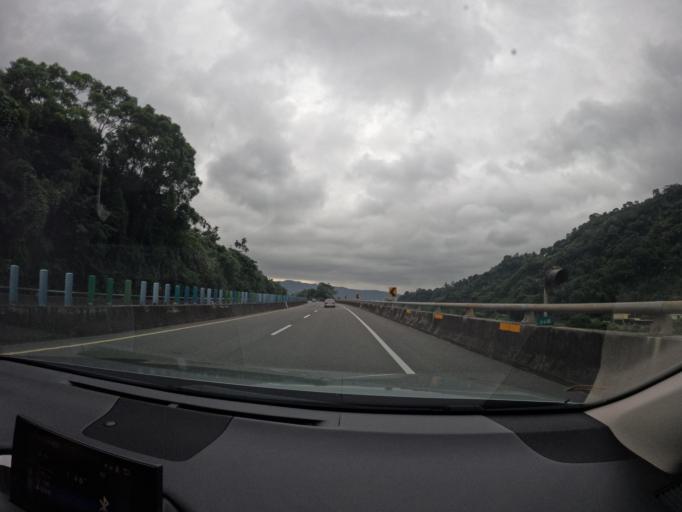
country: TW
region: Taiwan
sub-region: Miaoli
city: Miaoli
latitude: 24.4649
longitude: 120.8427
